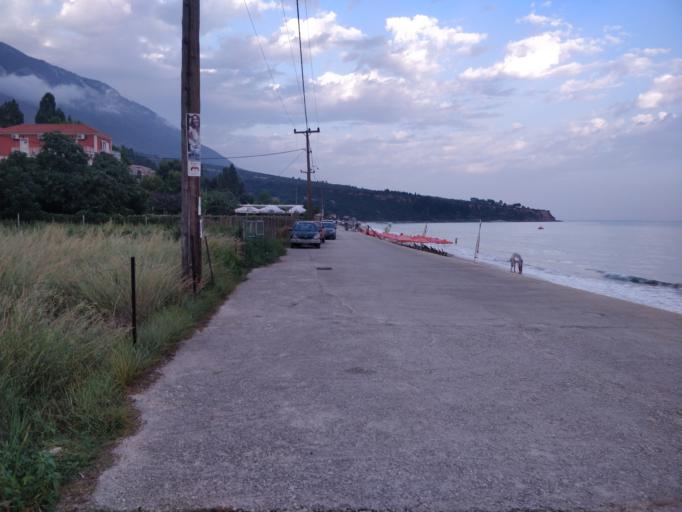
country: GR
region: Ionian Islands
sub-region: Nomos Kefallinias
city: Valsamata
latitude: 38.1137
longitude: 20.6328
